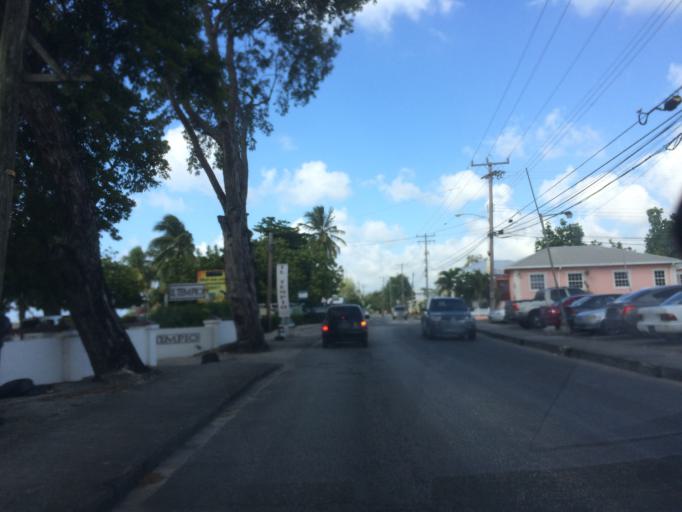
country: BB
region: Saint James
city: Holetown
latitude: 13.1458
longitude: -59.6383
